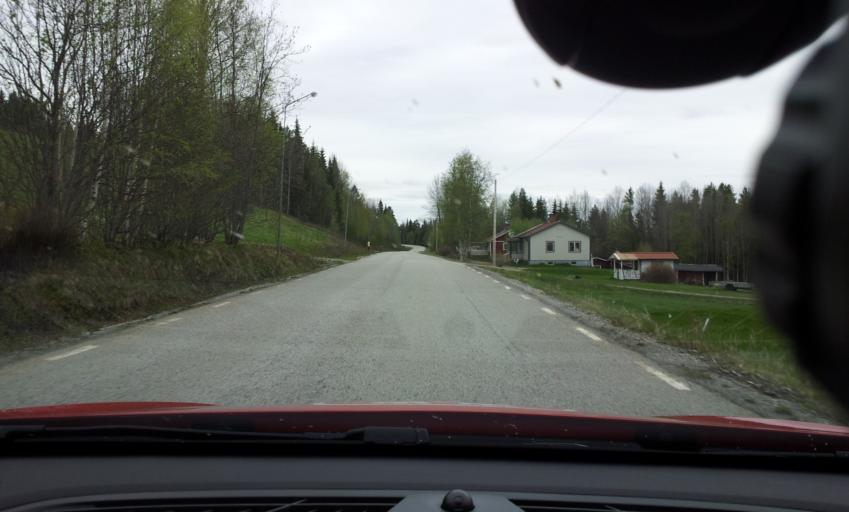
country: SE
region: Jaemtland
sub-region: Bergs Kommun
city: Hoverberg
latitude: 62.7243
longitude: 14.6003
